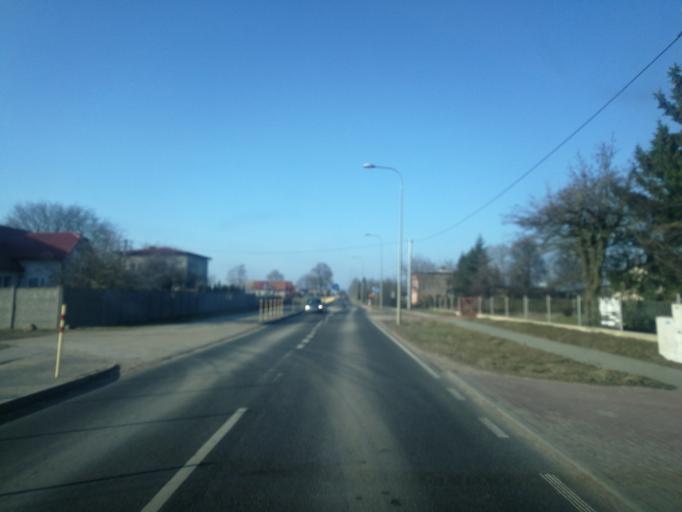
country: PL
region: Warmian-Masurian Voivodeship
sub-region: Powiat ilawski
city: Lubawa
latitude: 53.4652
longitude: 19.7728
